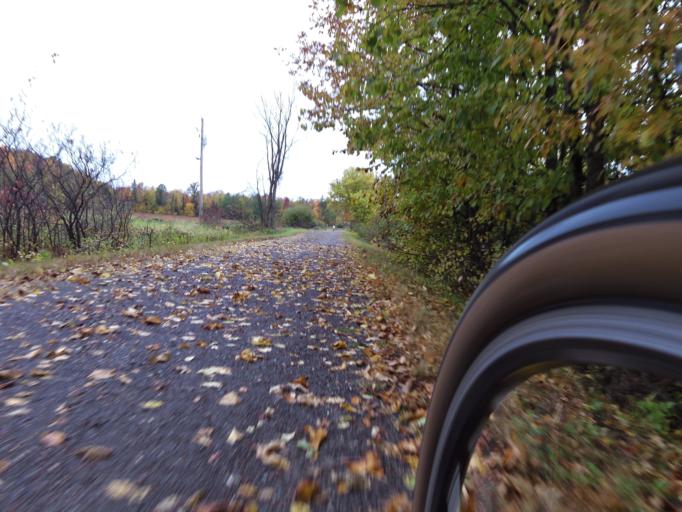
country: CA
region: Quebec
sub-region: Outaouais
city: Shawville
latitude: 45.6944
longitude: -76.5742
